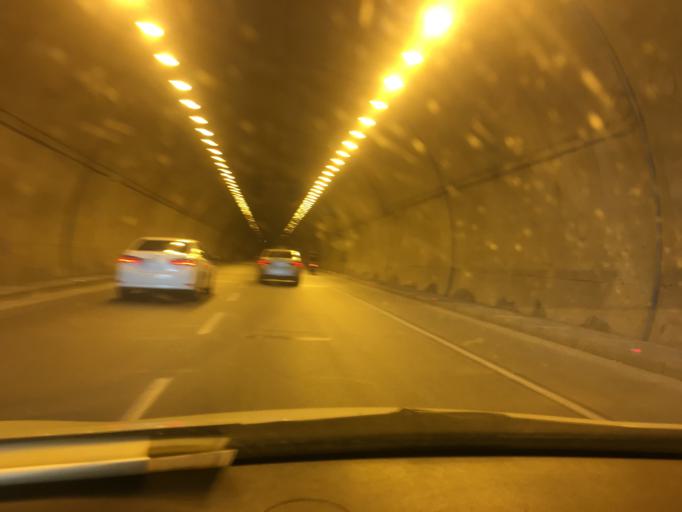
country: TR
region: Istanbul
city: Sisli
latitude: 41.0631
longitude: 28.9548
